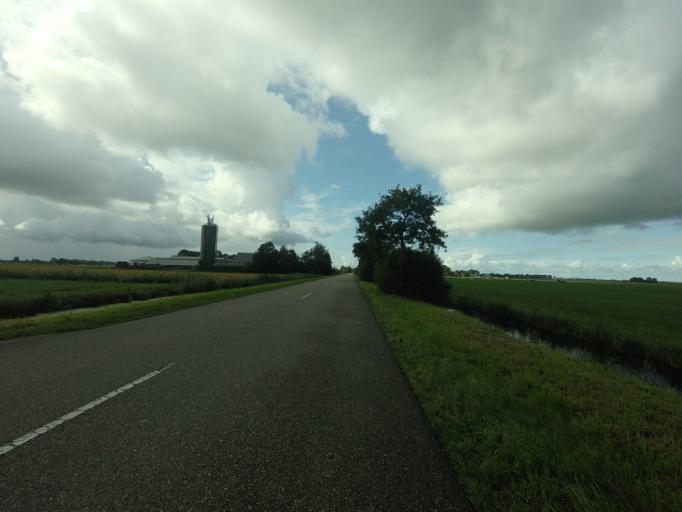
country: NL
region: Friesland
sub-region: Gemeente Boarnsterhim
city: Warten
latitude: 53.1552
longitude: 5.9121
